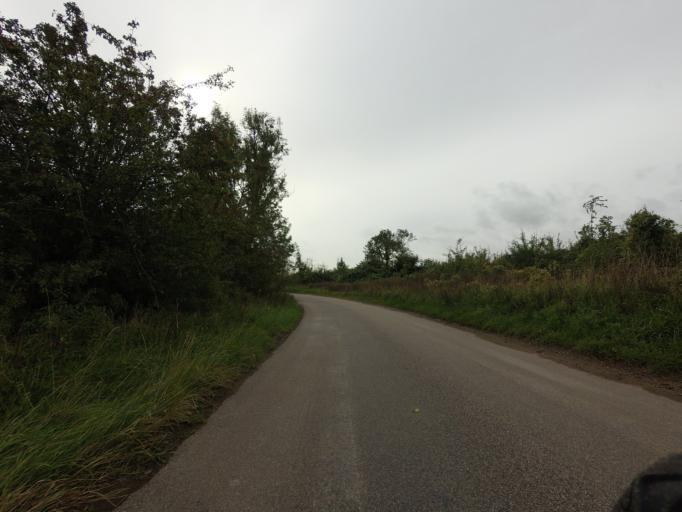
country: GB
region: England
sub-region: Hertfordshire
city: Reed
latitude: 51.9878
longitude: 0.0309
